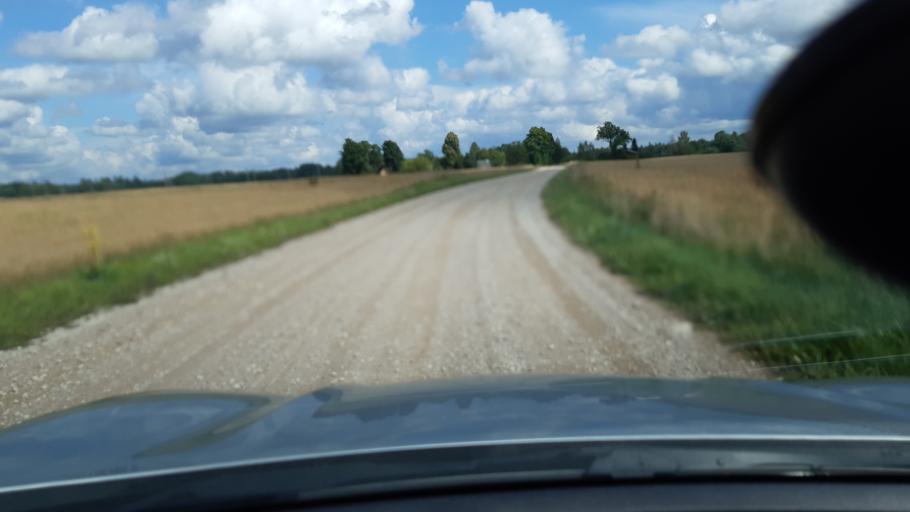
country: EE
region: Jaervamaa
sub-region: Tueri vald
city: Tueri
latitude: 58.9442
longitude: 25.2655
